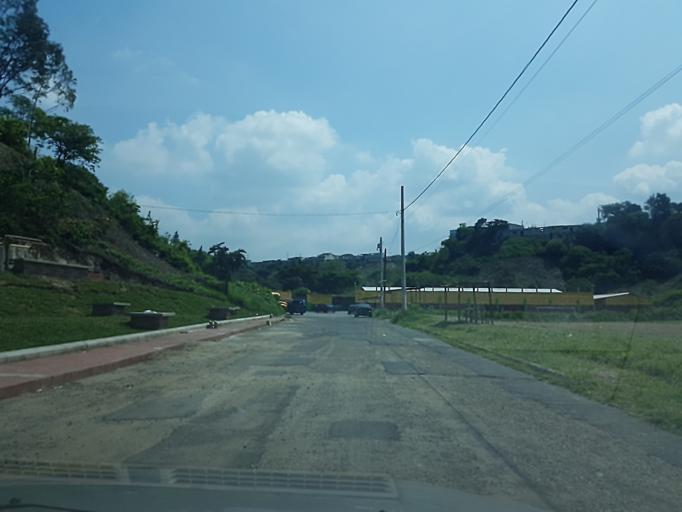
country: GT
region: Guatemala
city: Petapa
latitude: 14.5274
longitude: -90.5495
